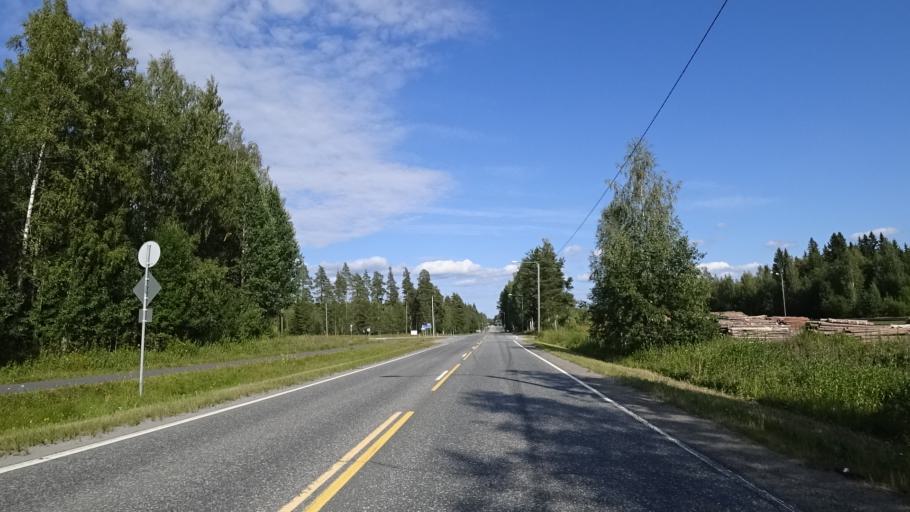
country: FI
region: North Karelia
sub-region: Joensuu
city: Eno
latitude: 62.8070
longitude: 30.1406
